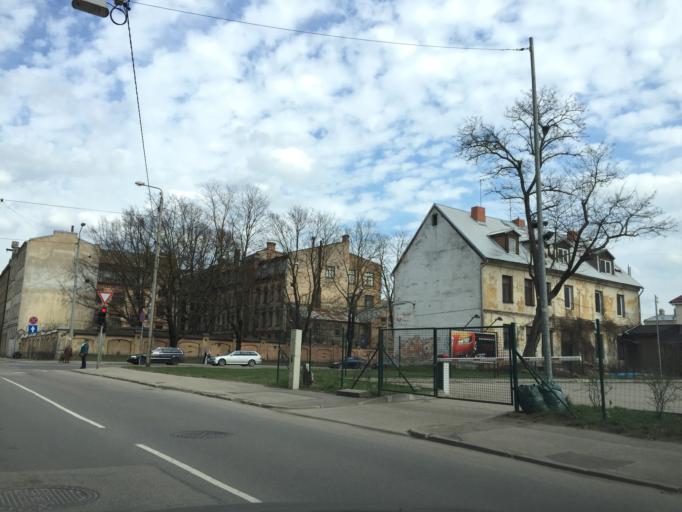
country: LV
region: Riga
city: Riga
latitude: 56.9408
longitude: 24.1201
